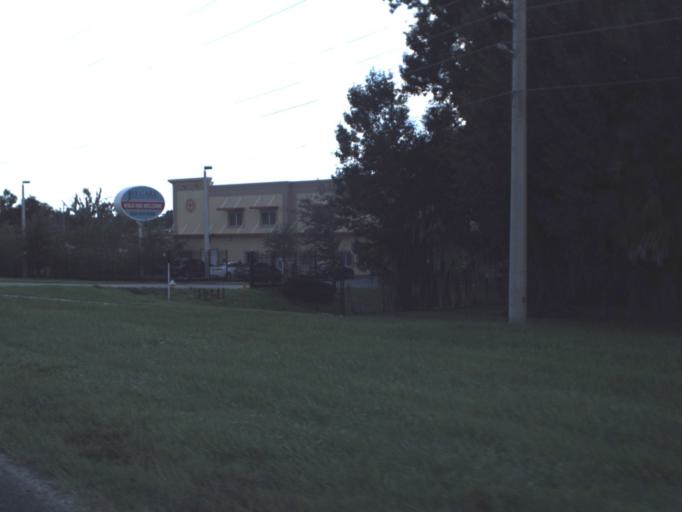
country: US
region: Florida
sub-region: Polk County
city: Medulla
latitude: 27.9593
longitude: -81.9669
